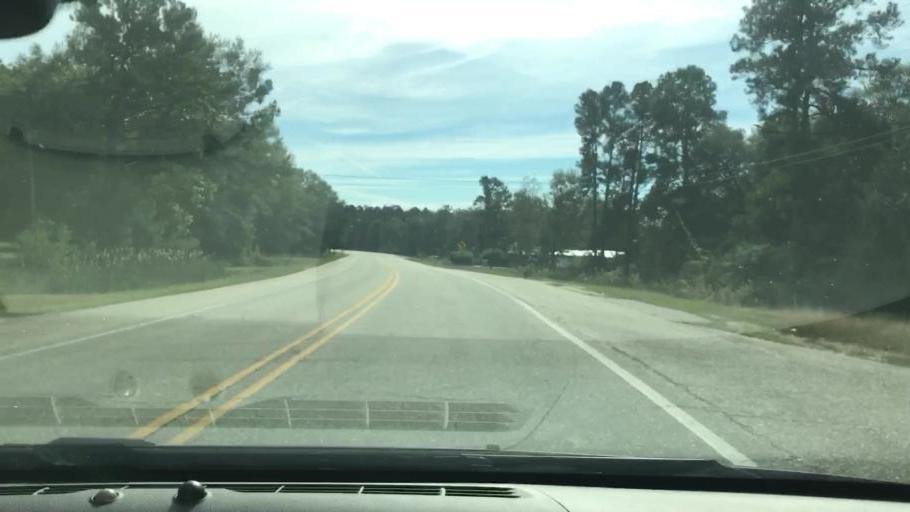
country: US
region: Louisiana
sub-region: Saint Tammany Parish
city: Pearl River
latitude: 30.4489
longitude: -89.7994
